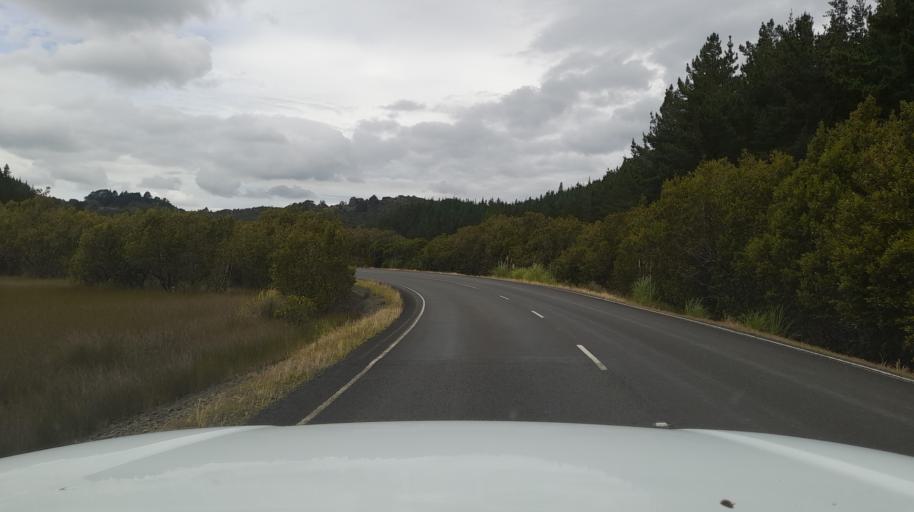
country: NZ
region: Northland
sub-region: Far North District
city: Kaitaia
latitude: -35.3638
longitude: 173.4399
